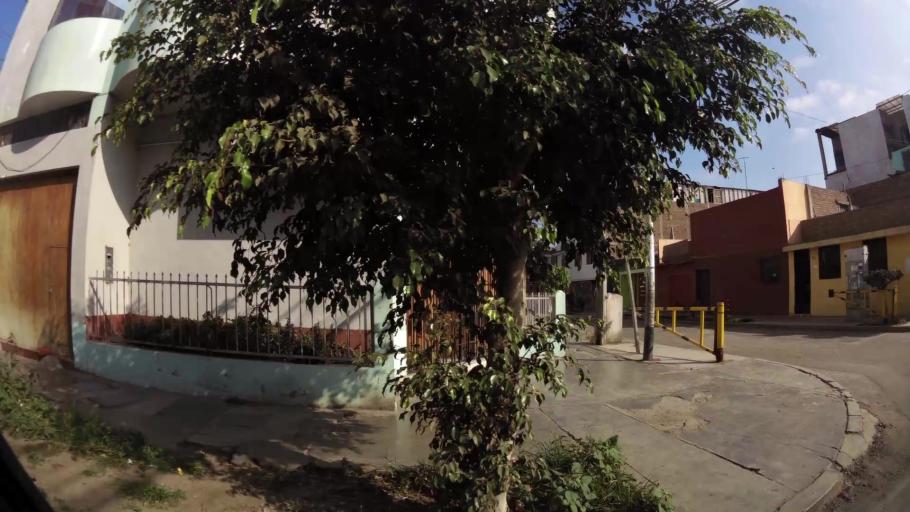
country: PE
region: La Libertad
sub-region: Provincia de Trujillo
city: Trujillo
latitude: -8.1100
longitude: -79.0047
